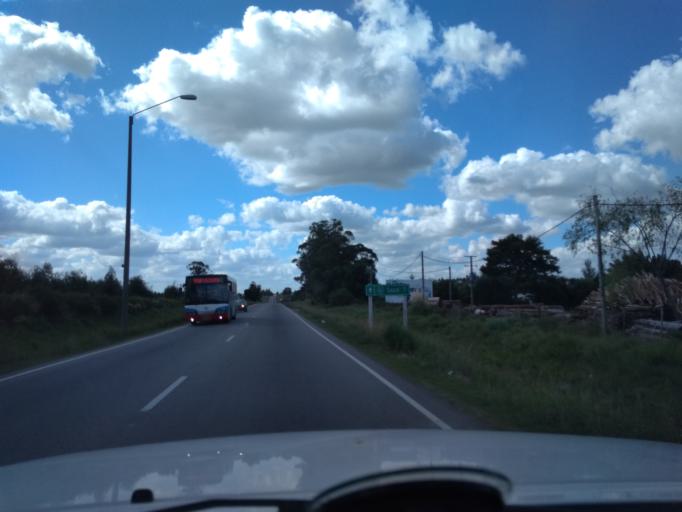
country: UY
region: Canelones
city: Joaquin Suarez
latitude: -34.7102
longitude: -56.0592
